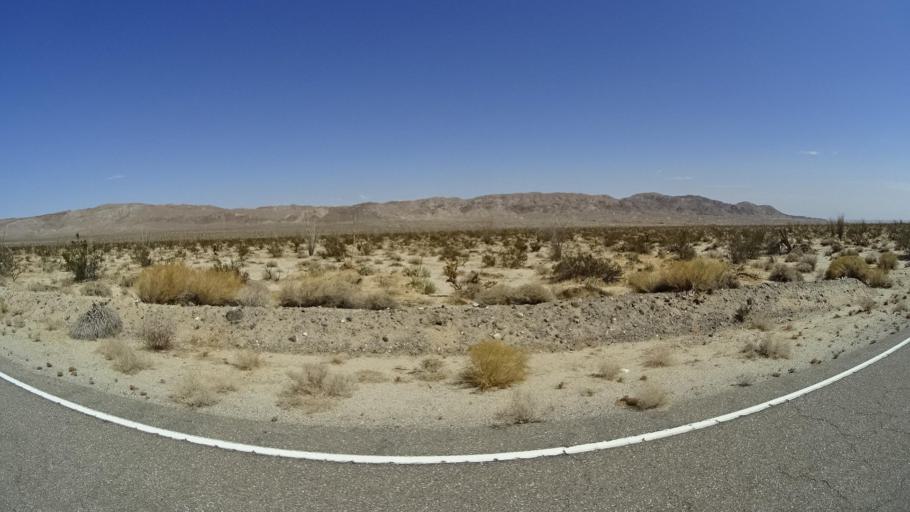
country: MX
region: Baja California
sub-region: Tecate
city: Cereso del Hongo
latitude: 32.7842
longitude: -116.0966
